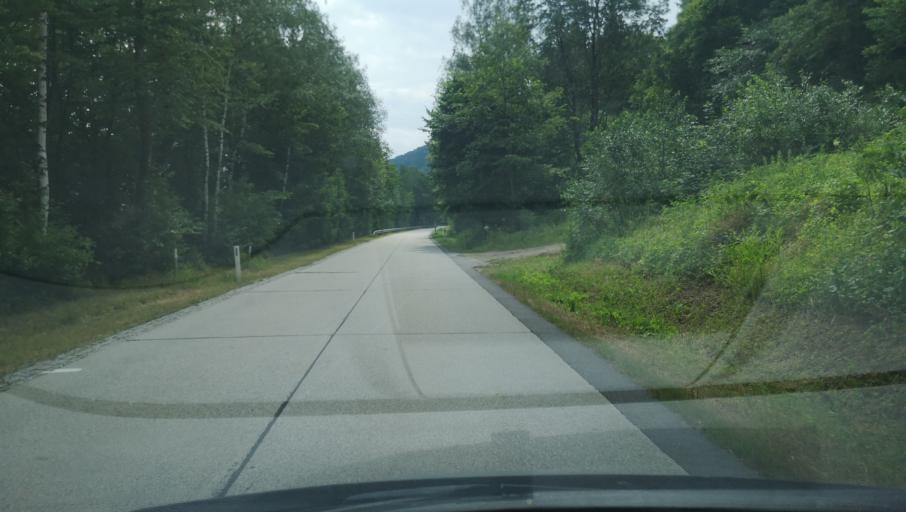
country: AT
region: Lower Austria
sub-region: Politischer Bezirk Melk
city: Nochling
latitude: 48.1934
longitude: 15.0024
